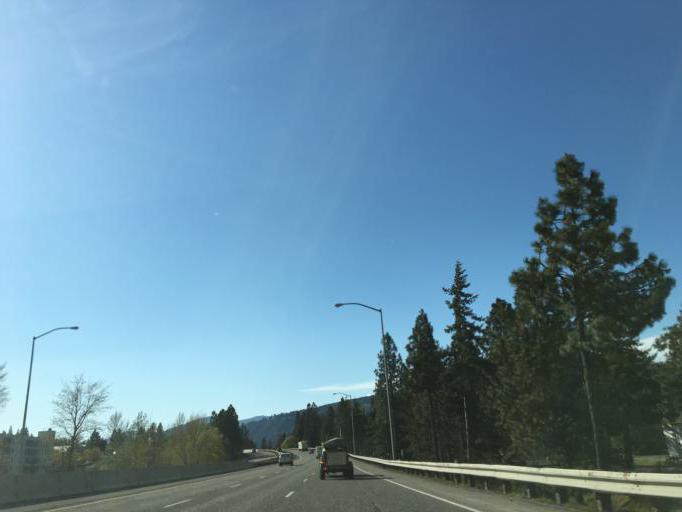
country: US
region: Oregon
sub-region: Hood River County
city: Hood River
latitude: 45.7118
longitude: -121.5160
